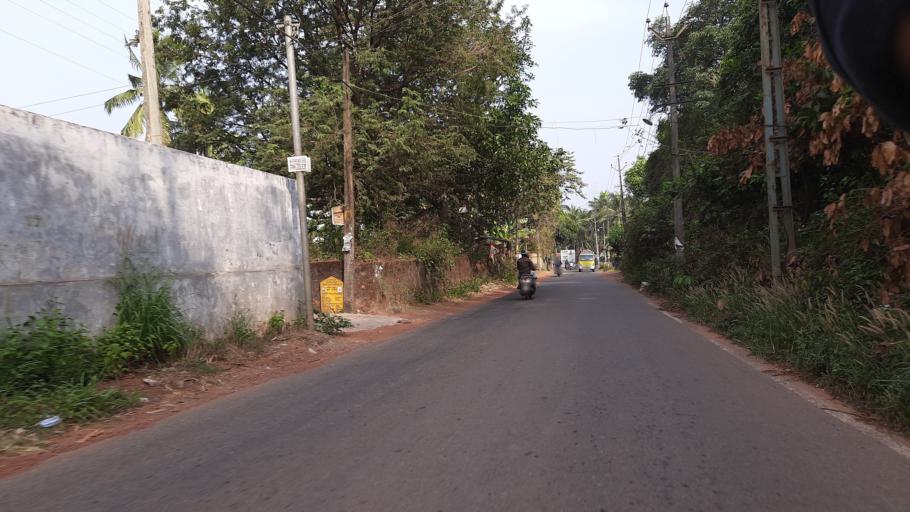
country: IN
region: Kerala
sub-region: Kozhikode
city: Ferokh
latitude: 11.1995
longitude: 75.8622
